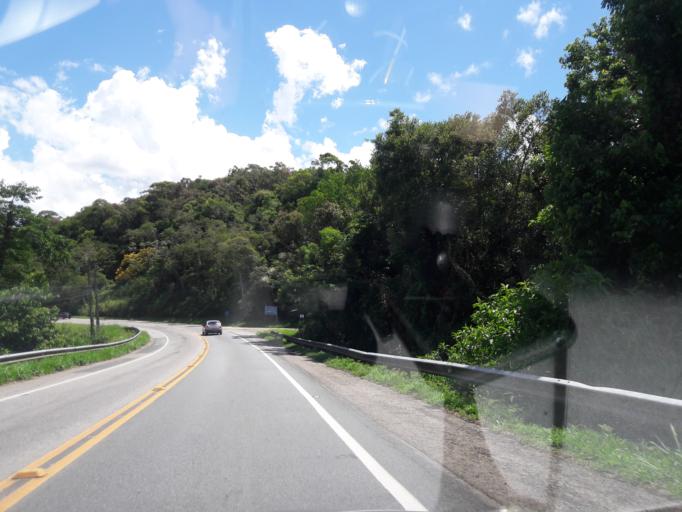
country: BR
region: Parana
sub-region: Antonina
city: Antonina
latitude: -25.4588
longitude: -48.8166
